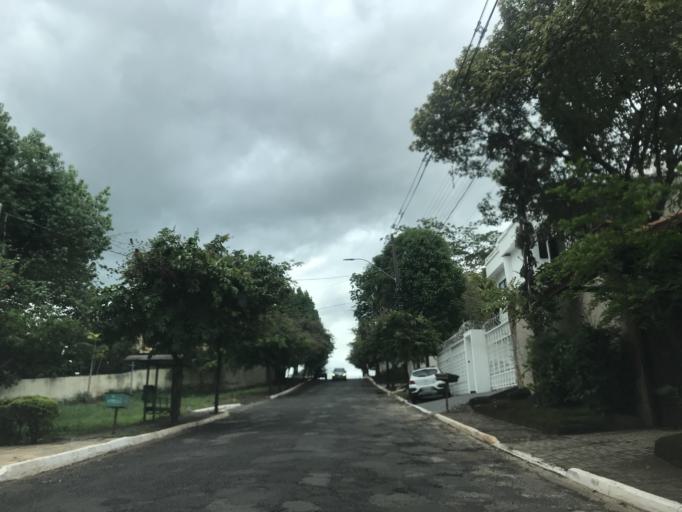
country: BR
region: Goias
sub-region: Caldas Novas
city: Caldas Novas
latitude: -17.7687
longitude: -48.7588
